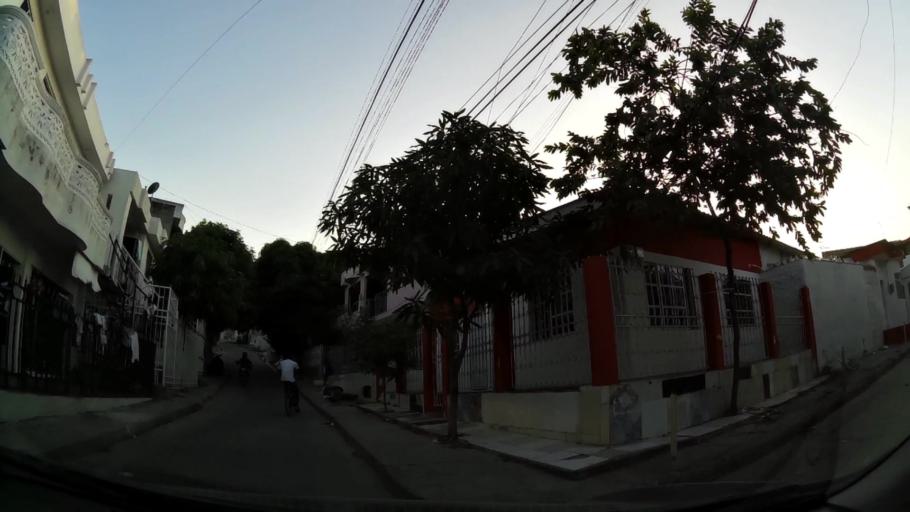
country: CO
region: Bolivar
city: Cartagena
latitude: 10.3863
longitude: -75.4900
